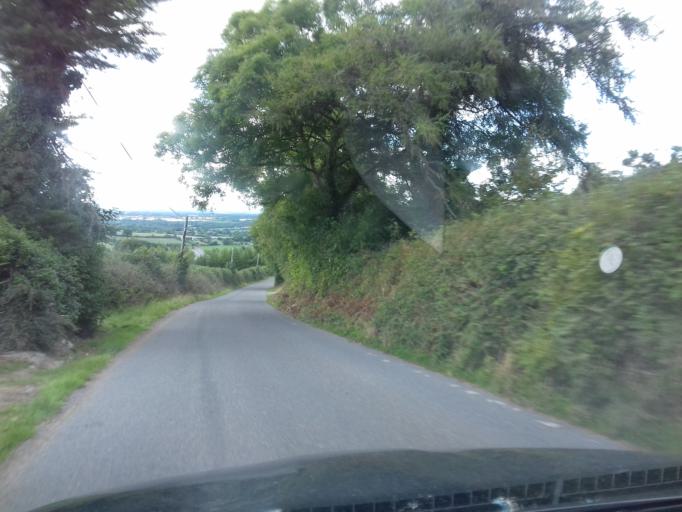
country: IE
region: Leinster
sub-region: Kilkenny
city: Graiguenamanagh
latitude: 52.5780
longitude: -7.0104
